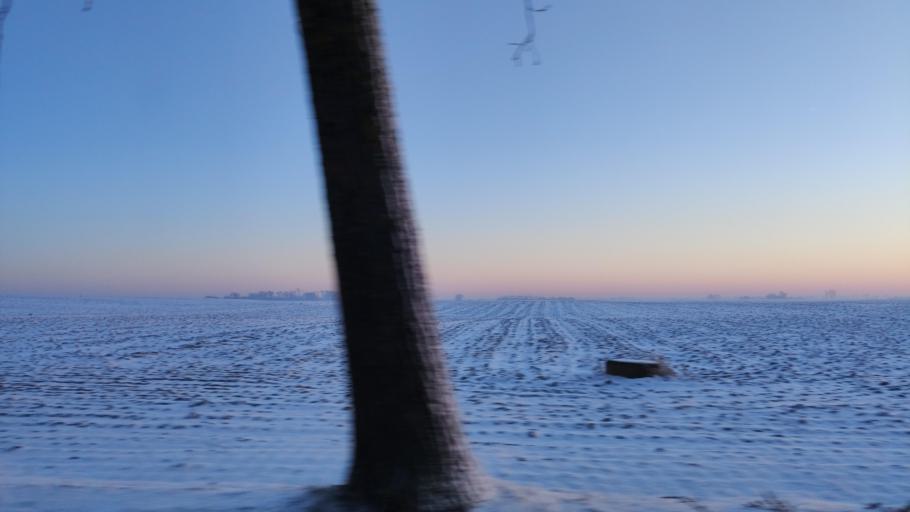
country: PL
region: Kujawsko-Pomorskie
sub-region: Powiat zninski
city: Znin
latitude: 52.8708
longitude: 17.8296
